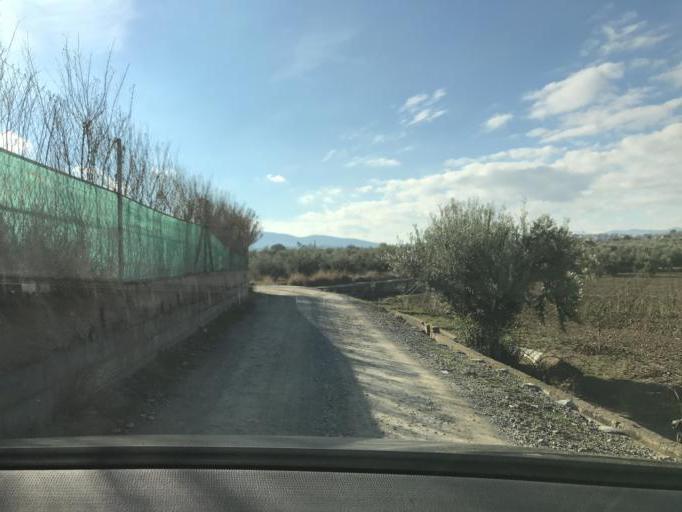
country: ES
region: Andalusia
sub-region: Provincia de Granada
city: Gojar
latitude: 37.1070
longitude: -3.6248
